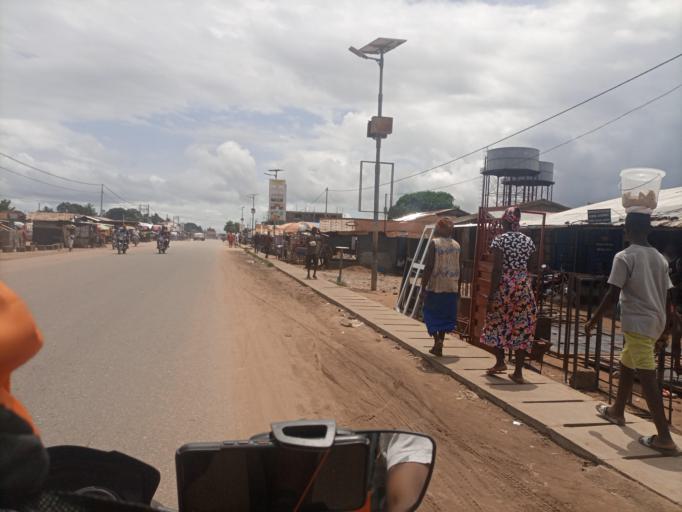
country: SL
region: Northern Province
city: Masoyila
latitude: 8.6033
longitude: -13.1788
